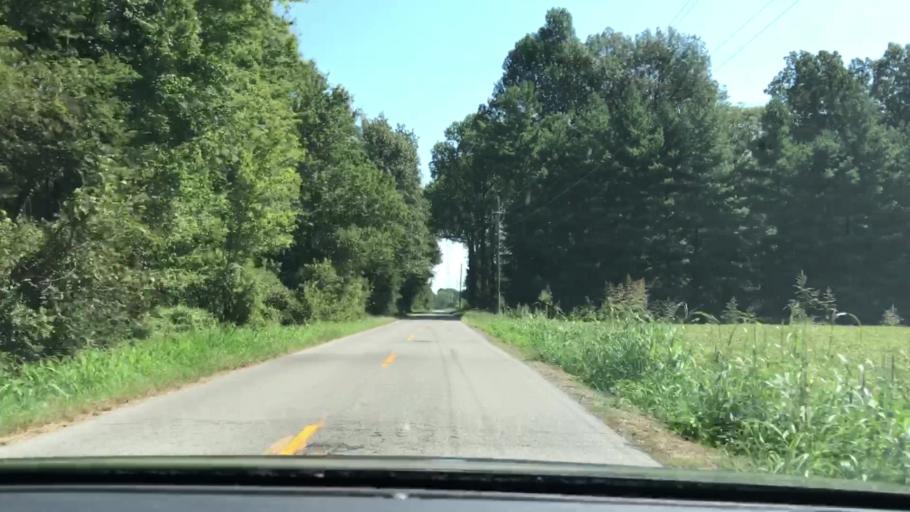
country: US
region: Kentucky
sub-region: Fulton County
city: Fulton
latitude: 36.5220
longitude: -88.8976
